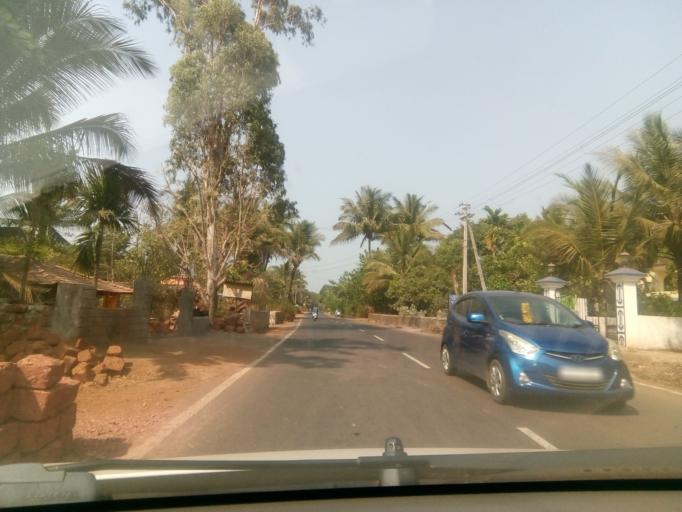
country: IN
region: Goa
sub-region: North Goa
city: Pernem
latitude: 15.6943
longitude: 73.8435
